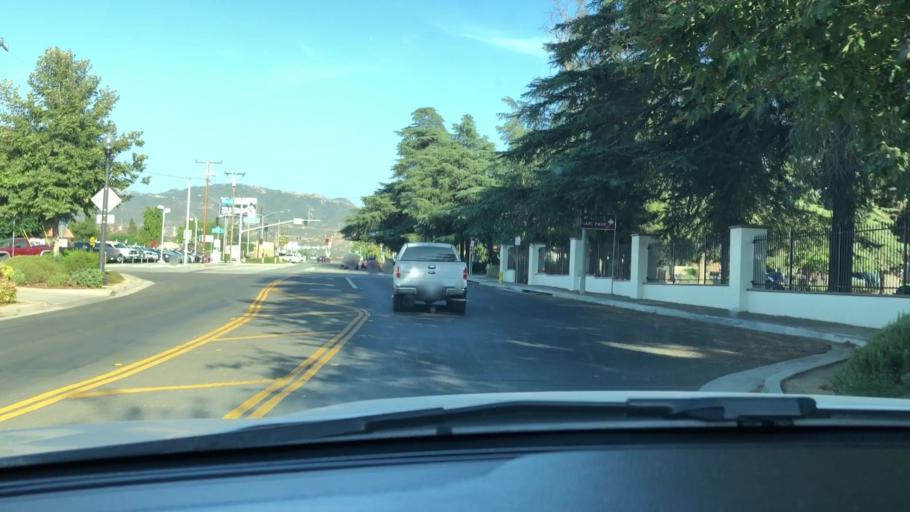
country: US
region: California
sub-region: Los Angeles County
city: Santa Clarita
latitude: 34.3763
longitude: -118.5259
